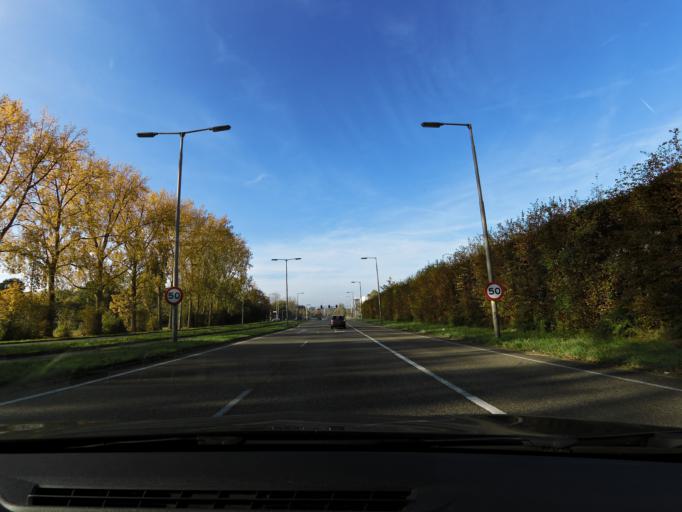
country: NL
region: South Holland
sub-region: Gemeente Ridderkerk
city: Ridderkerk
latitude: 51.8794
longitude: 4.5950
